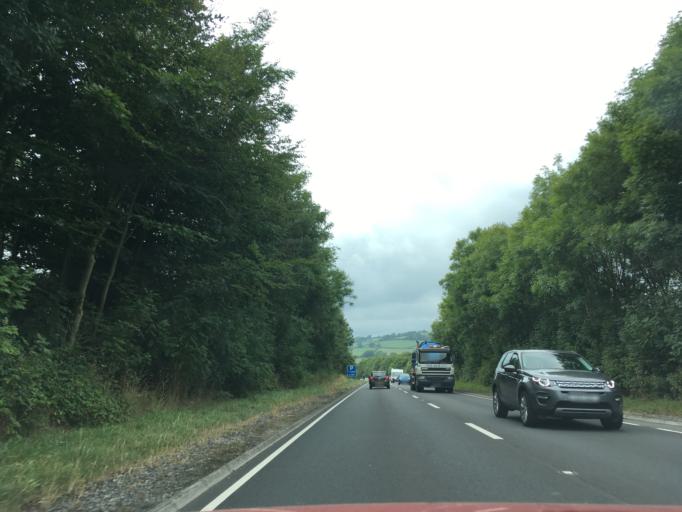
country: GB
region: Wales
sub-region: Carmarthenshire
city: Llanddowror
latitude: 51.8253
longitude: -4.5495
